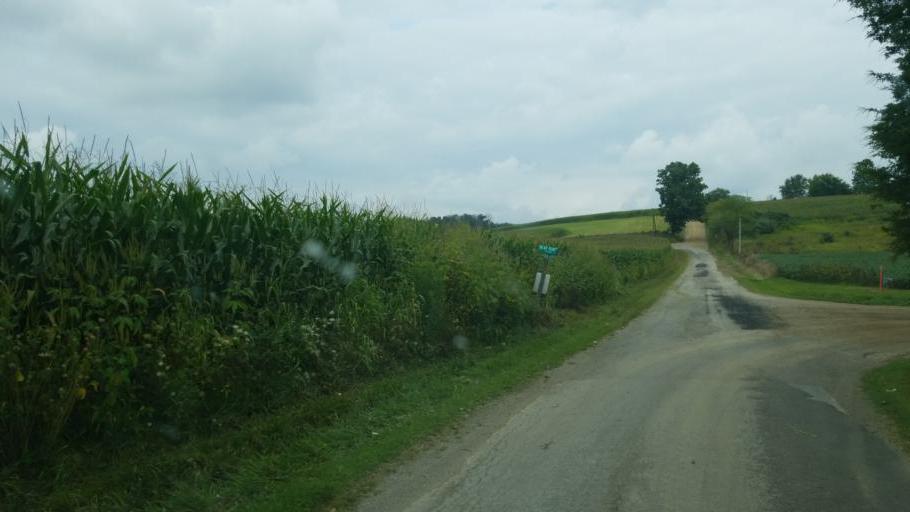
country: US
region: Ohio
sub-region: Knox County
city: Danville
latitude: 40.5078
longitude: -82.3057
